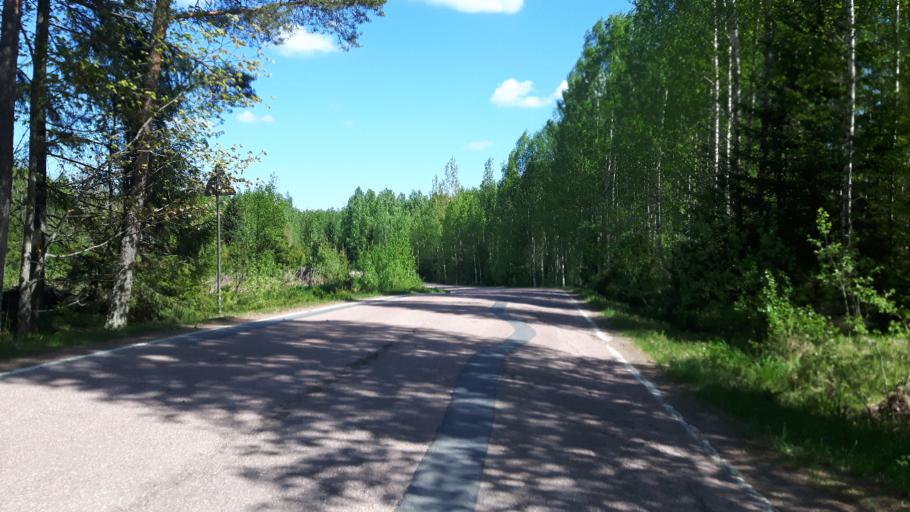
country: FI
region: Kymenlaakso
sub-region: Kotka-Hamina
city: Virolahti
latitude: 60.5404
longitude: 27.6262
